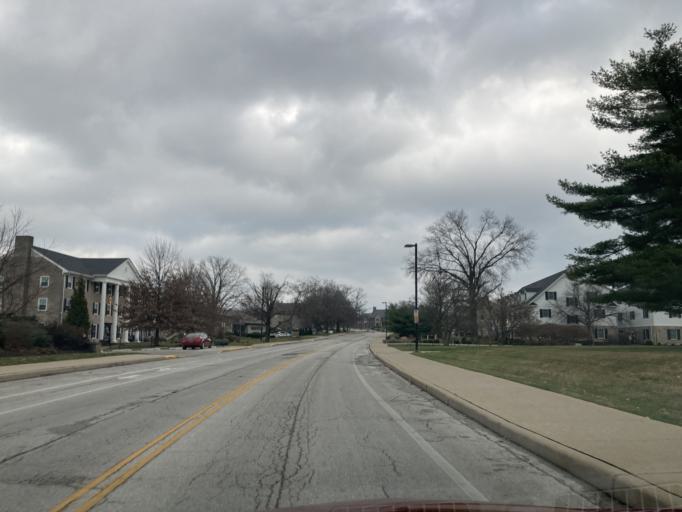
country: US
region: Indiana
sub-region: Monroe County
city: Bloomington
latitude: 39.1741
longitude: -86.5151
